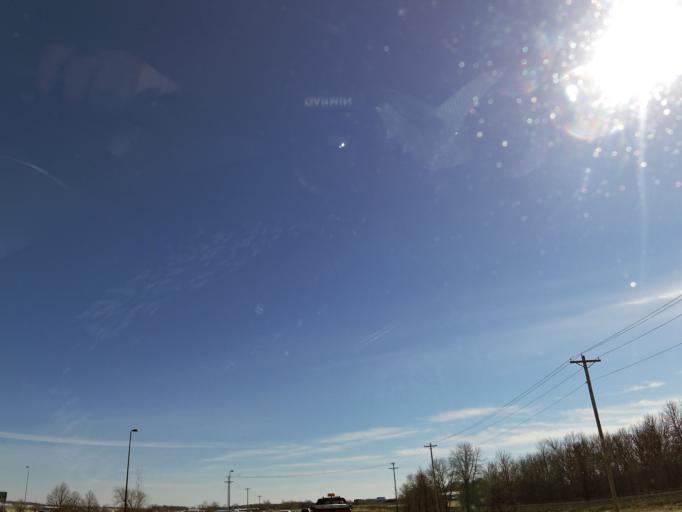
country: US
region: Minnesota
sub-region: Wright County
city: Buffalo
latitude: 45.1648
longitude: -93.8583
